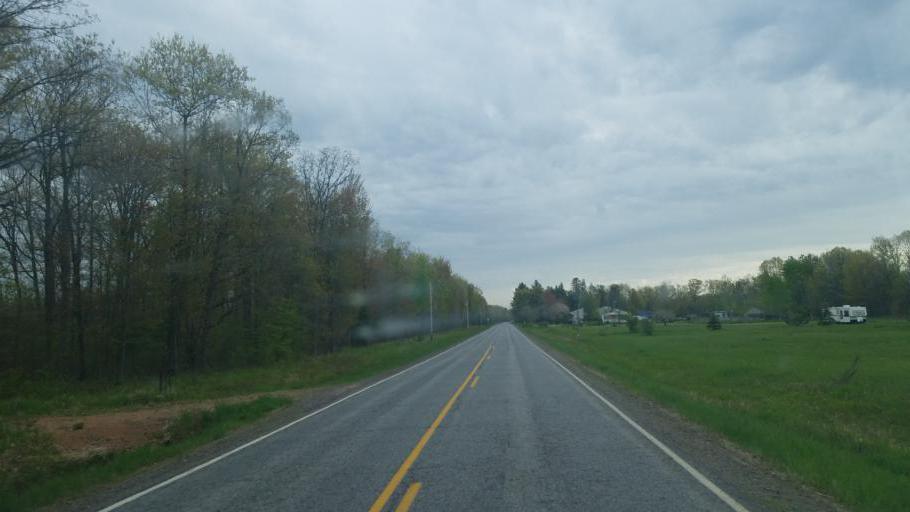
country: US
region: Wisconsin
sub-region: Wood County
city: Marshfield
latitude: 44.4022
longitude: -90.1603
